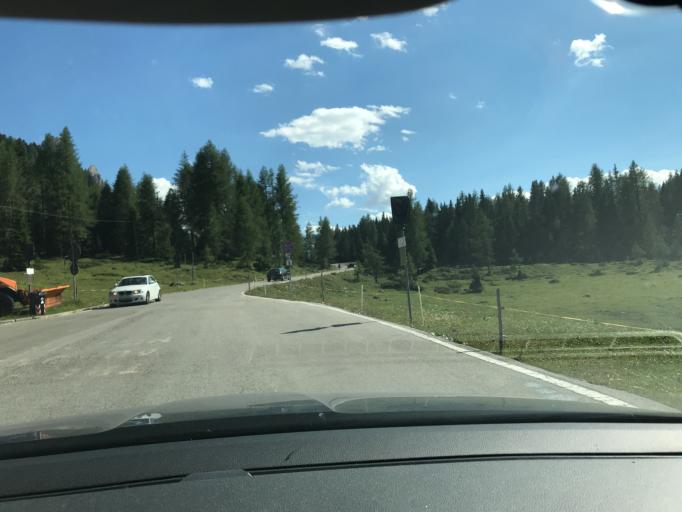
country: IT
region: Trentino-Alto Adige
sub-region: Bolzano
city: Sesto
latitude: 46.5995
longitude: 12.2698
